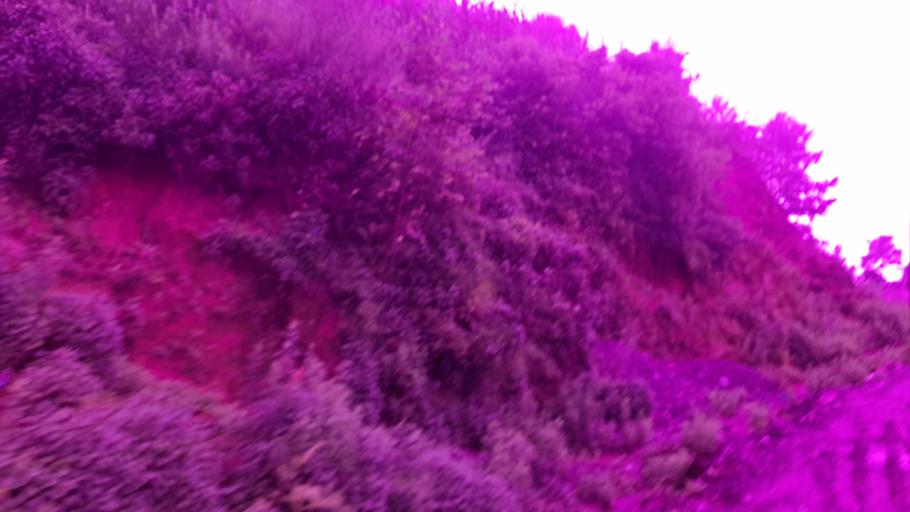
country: NP
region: Central Region
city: Kirtipur
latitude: 27.8208
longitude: 85.2252
